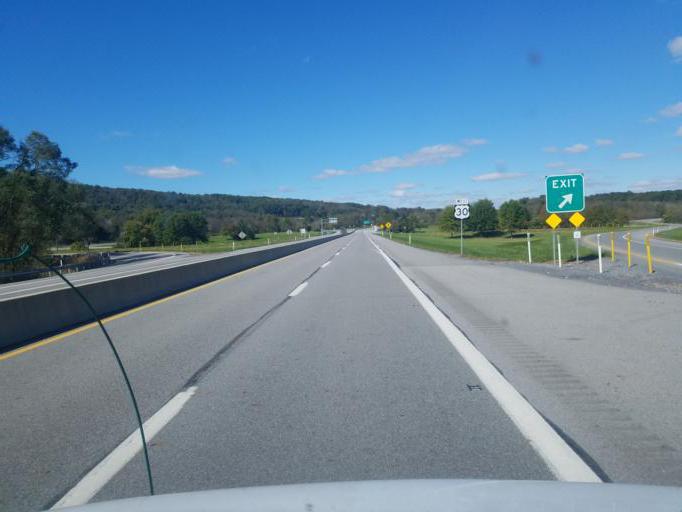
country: US
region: Pennsylvania
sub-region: Bedford County
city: Bedford
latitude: 40.0235
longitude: -78.5103
